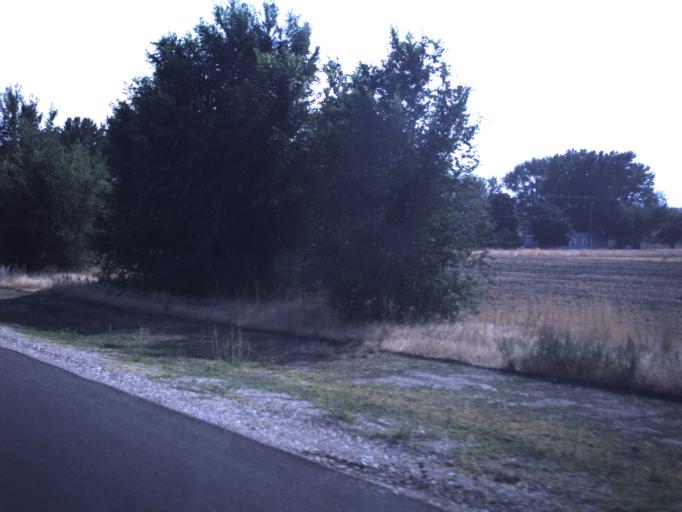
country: US
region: Utah
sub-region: Box Elder County
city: South Willard
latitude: 41.3525
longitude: -112.0361
